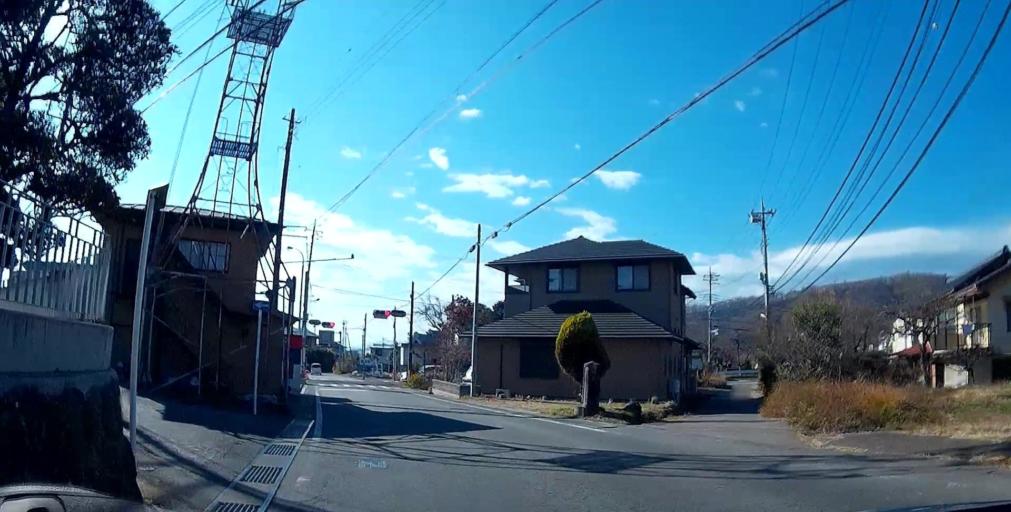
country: JP
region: Yamanashi
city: Enzan
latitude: 35.7251
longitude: 138.7152
